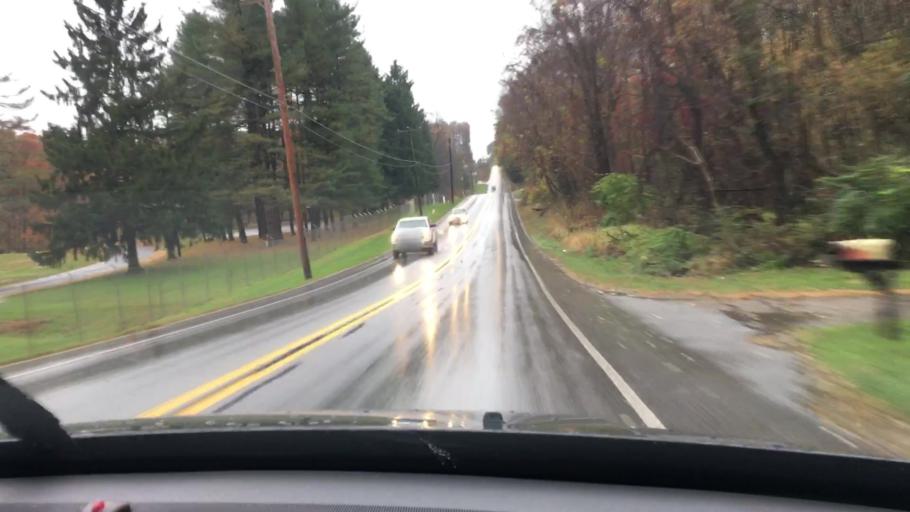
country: US
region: Pennsylvania
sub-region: Lancaster County
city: Conestoga
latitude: 39.8544
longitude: -76.2851
